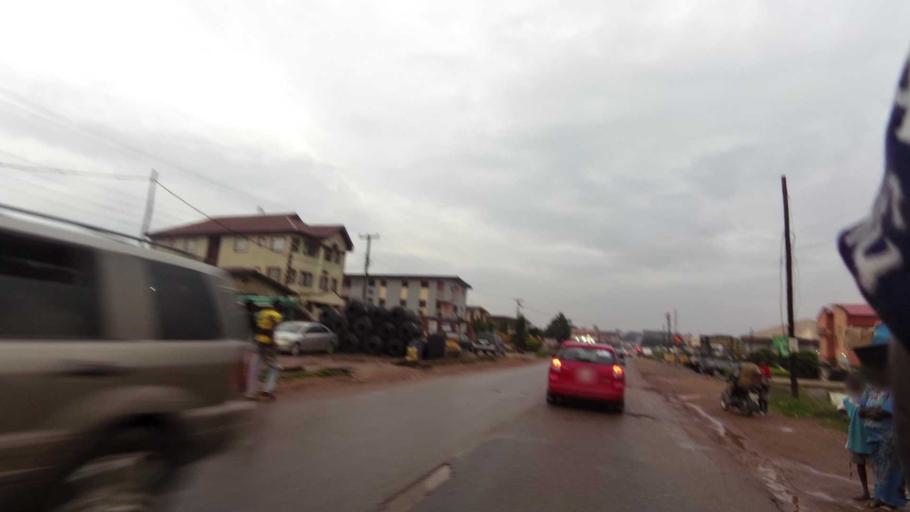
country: NG
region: Oyo
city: Ibadan
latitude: 7.4338
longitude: 3.9431
